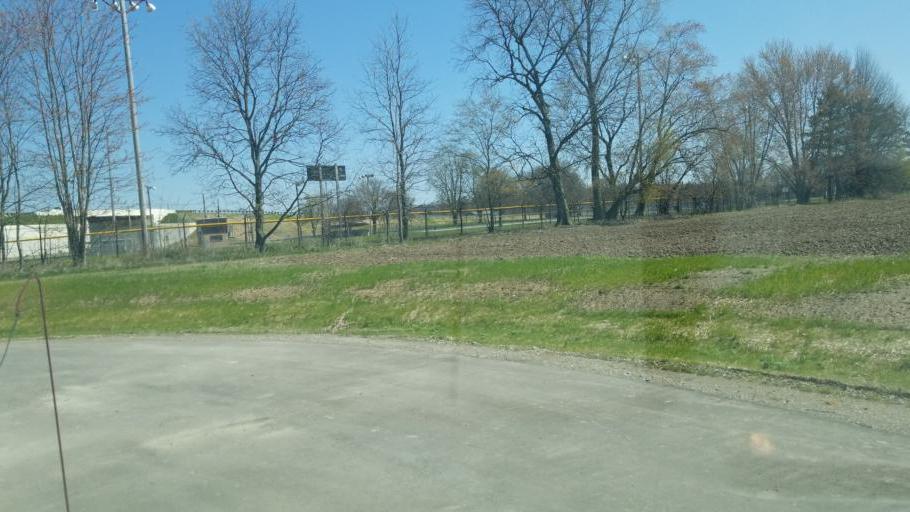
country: US
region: Ohio
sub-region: Marion County
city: Marion
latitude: 40.6005
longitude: -83.0709
